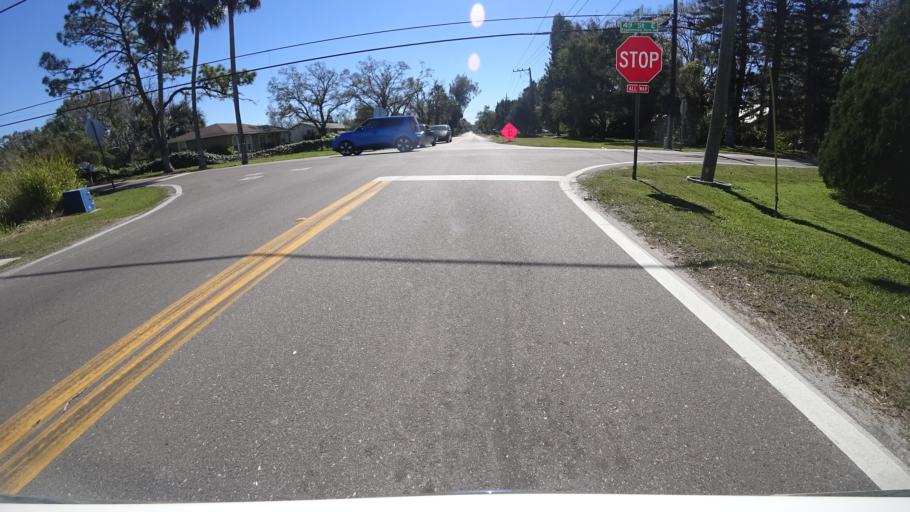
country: US
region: Florida
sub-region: Manatee County
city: Memphis
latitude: 27.5581
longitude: -82.5482
